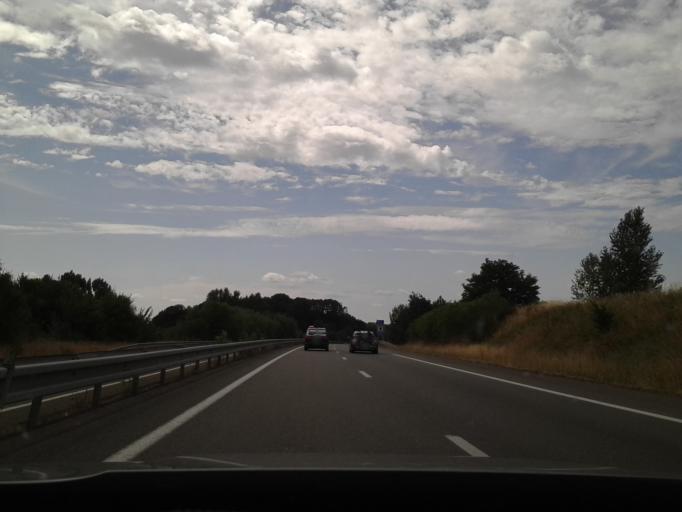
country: FR
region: Pays de la Loire
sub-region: Departement de la Sarthe
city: La Bazoge
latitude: 48.0916
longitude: 0.1755
